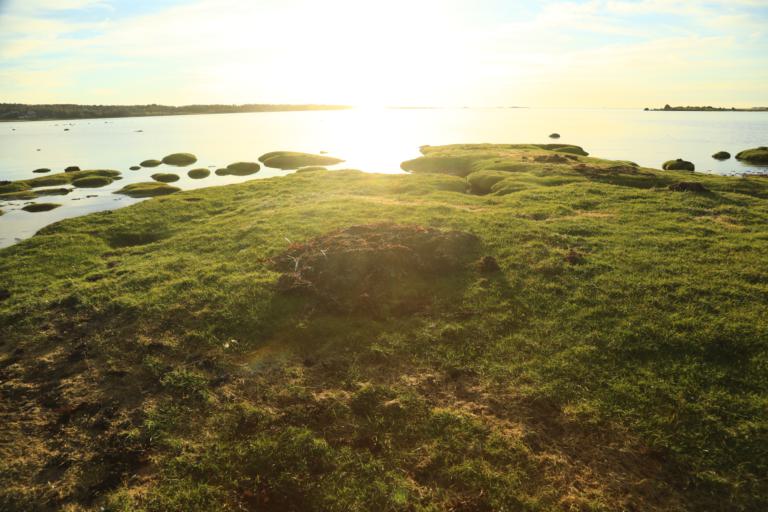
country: SE
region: Halland
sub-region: Varbergs Kommun
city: Varberg
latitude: 57.1626
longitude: 12.2267
